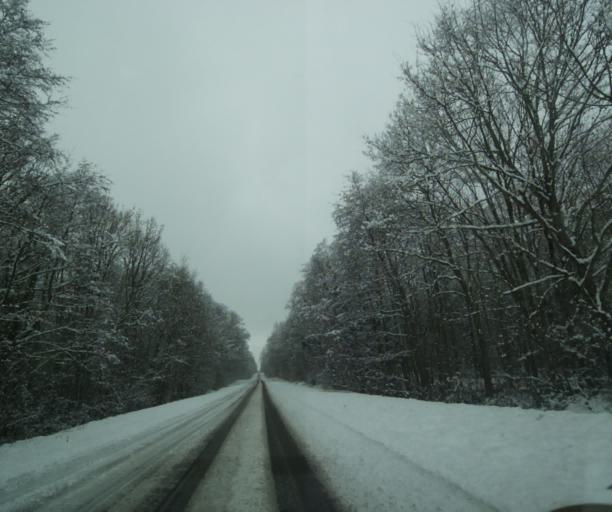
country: FR
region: Champagne-Ardenne
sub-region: Departement de la Haute-Marne
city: Montier-en-Der
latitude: 48.5247
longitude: 4.8010
